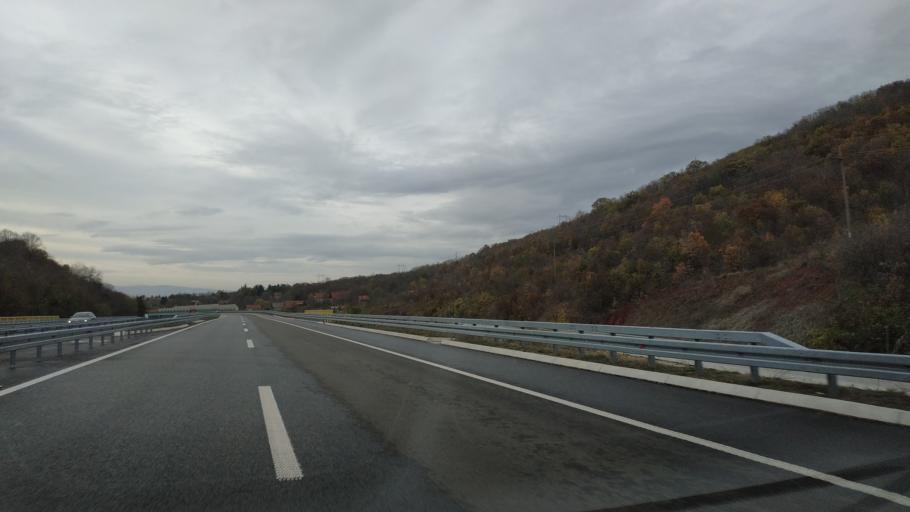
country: RS
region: Central Serbia
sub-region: Nisavski Okrug
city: Niska Banja
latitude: 43.2997
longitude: 22.0638
